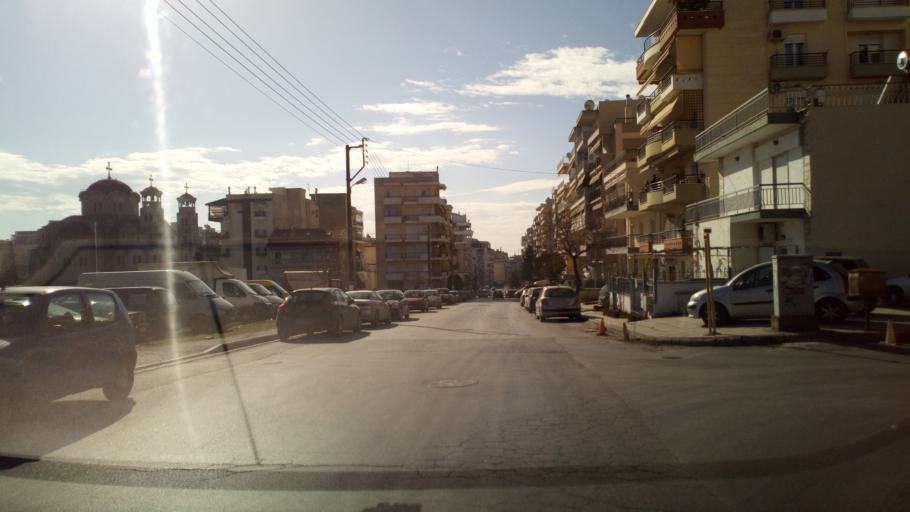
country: GR
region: Central Macedonia
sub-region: Nomos Thessalonikis
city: Evosmos
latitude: 40.6762
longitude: 22.9085
